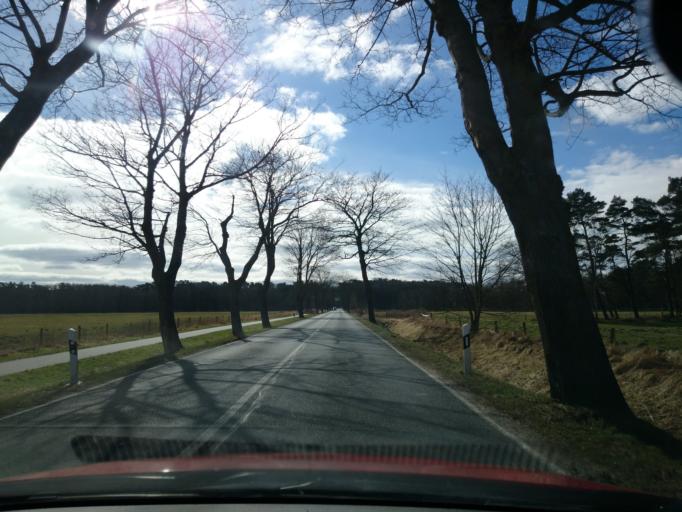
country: DE
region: Mecklenburg-Vorpommern
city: Ostseebad Prerow
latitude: 54.4369
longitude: 12.5769
